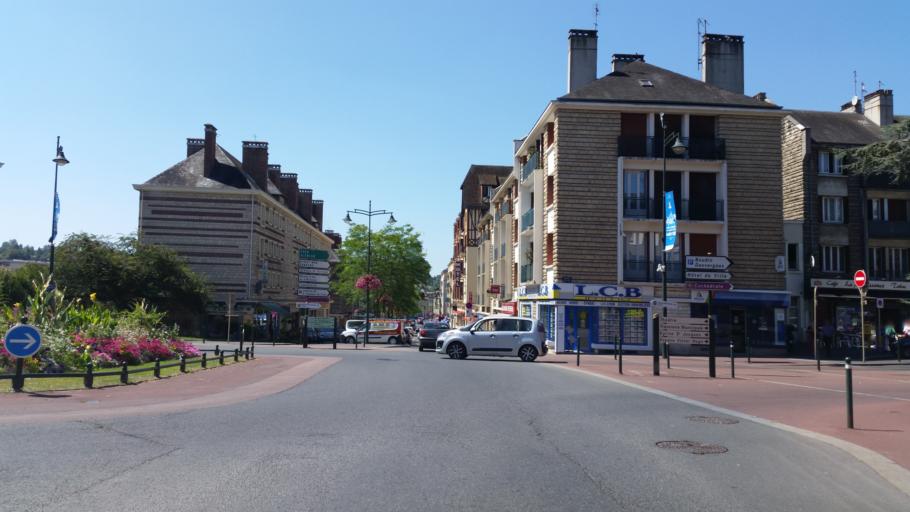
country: FR
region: Lower Normandy
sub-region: Departement du Calvados
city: Lisieux
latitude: 49.1437
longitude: 0.2293
